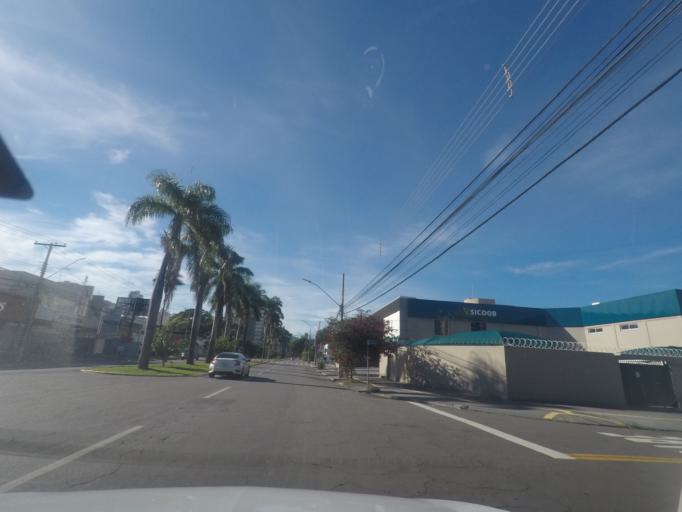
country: BR
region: Goias
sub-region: Goiania
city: Goiania
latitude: -16.6737
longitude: -49.2690
